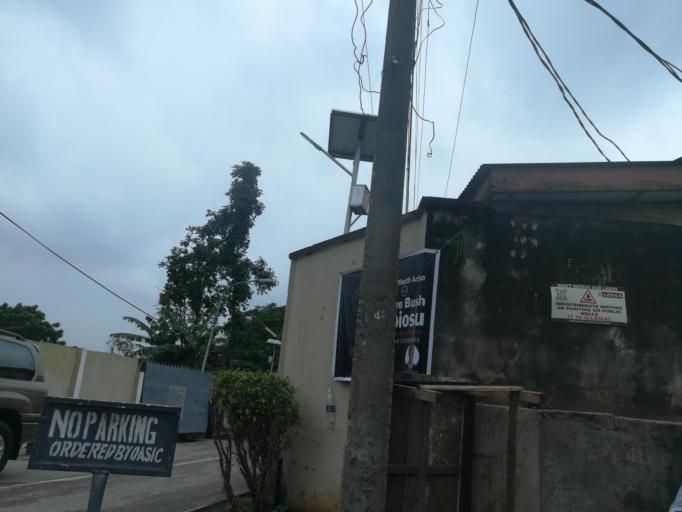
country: NG
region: Lagos
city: Ojota
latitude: 6.5690
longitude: 3.3732
